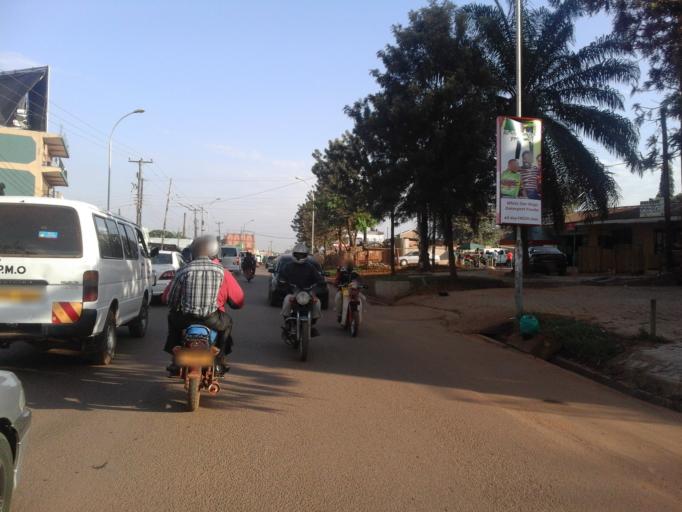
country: UG
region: Central Region
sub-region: Kampala District
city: Kampala
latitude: 0.2870
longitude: 32.6074
